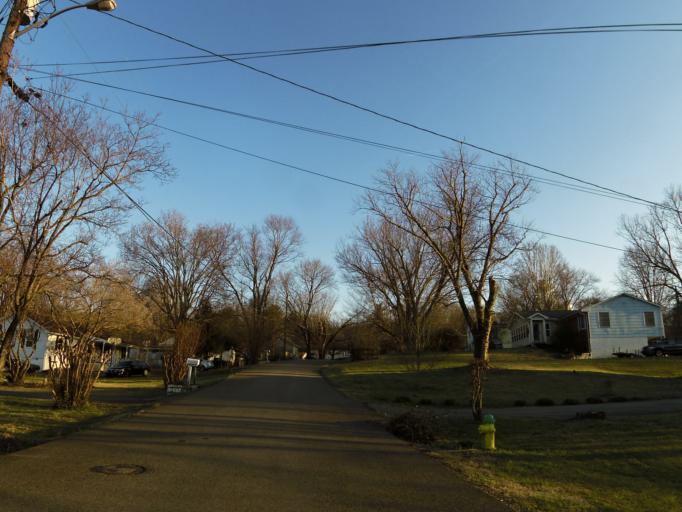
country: US
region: Tennessee
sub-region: Knox County
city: Knoxville
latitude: 36.0169
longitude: -83.8941
